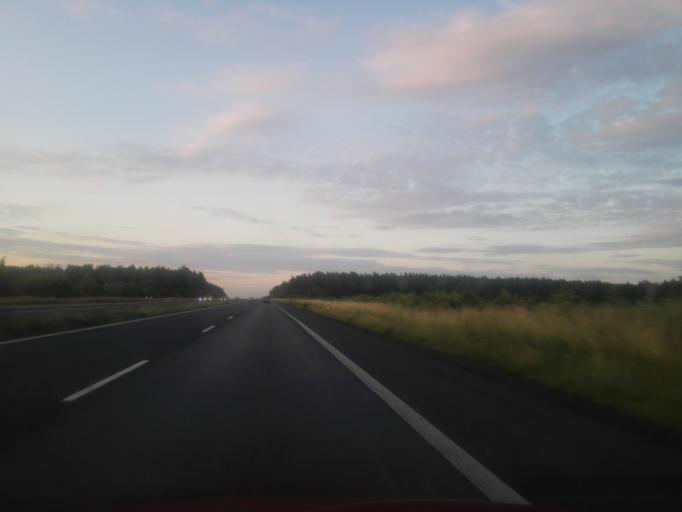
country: PL
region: Silesian Voivodeship
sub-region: Powiat czestochowski
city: Borowno
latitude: 50.9779
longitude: 19.2744
